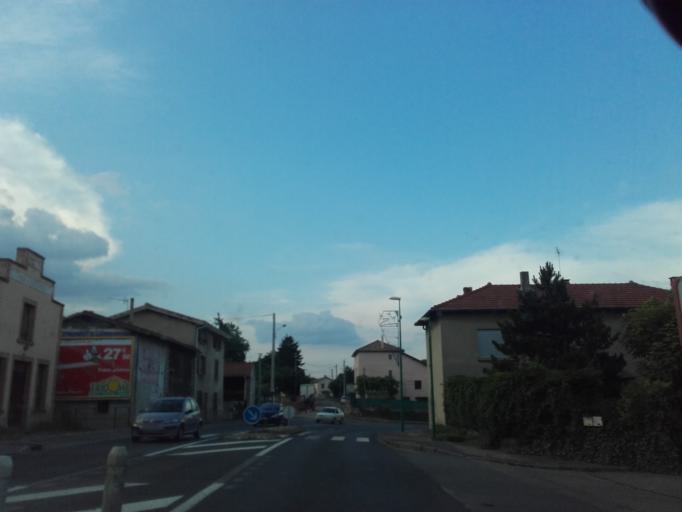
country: FR
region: Rhone-Alpes
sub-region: Departement de l'Isere
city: Reventin-Vaugris
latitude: 45.4788
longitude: 4.8297
